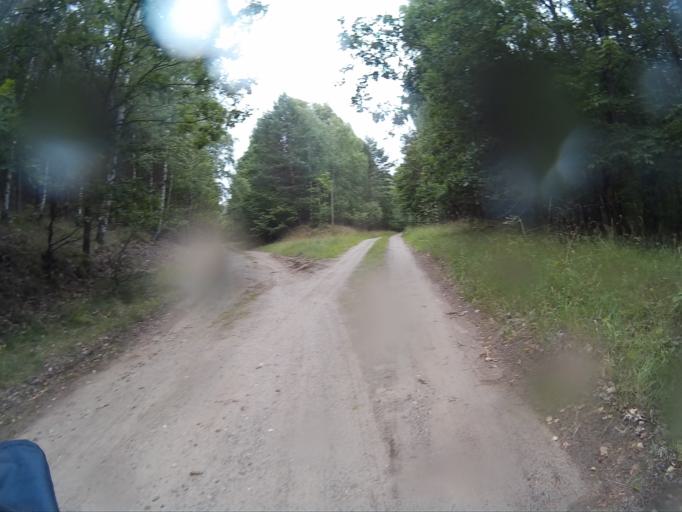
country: PL
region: Kujawsko-Pomorskie
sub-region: Powiat tucholski
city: Tuchola
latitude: 53.6009
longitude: 17.9231
